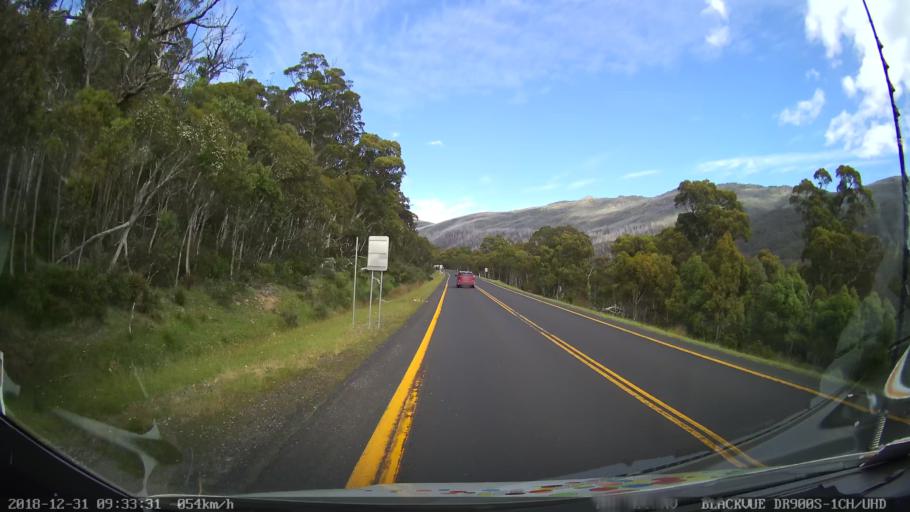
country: AU
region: New South Wales
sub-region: Snowy River
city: Jindabyne
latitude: -36.4504
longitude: 148.4221
